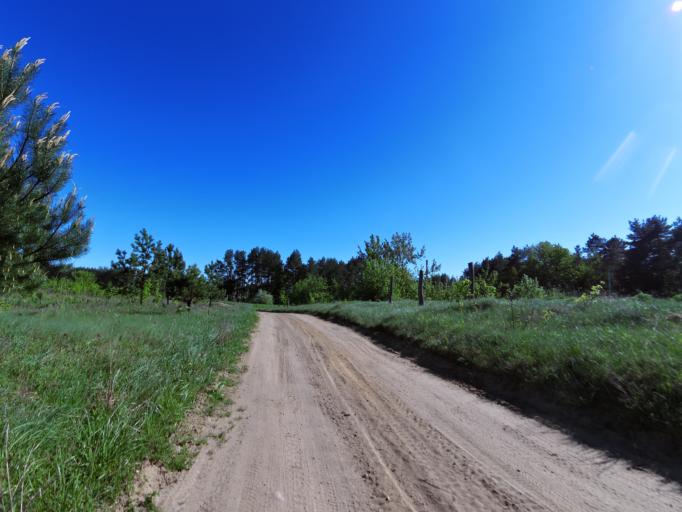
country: LT
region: Vilnius County
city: Pilaite
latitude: 54.6853
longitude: 25.1610
